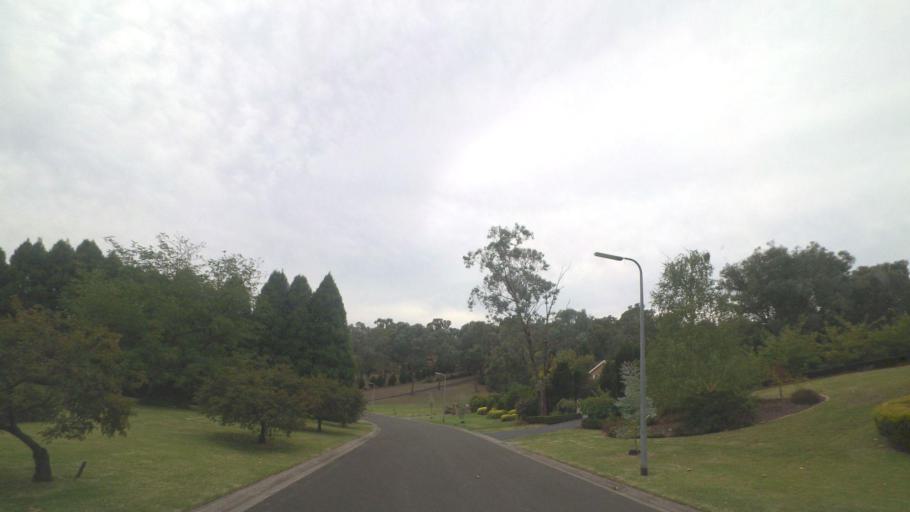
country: AU
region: Victoria
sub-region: Nillumbik
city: North Warrandyte
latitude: -37.7459
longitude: 145.1918
